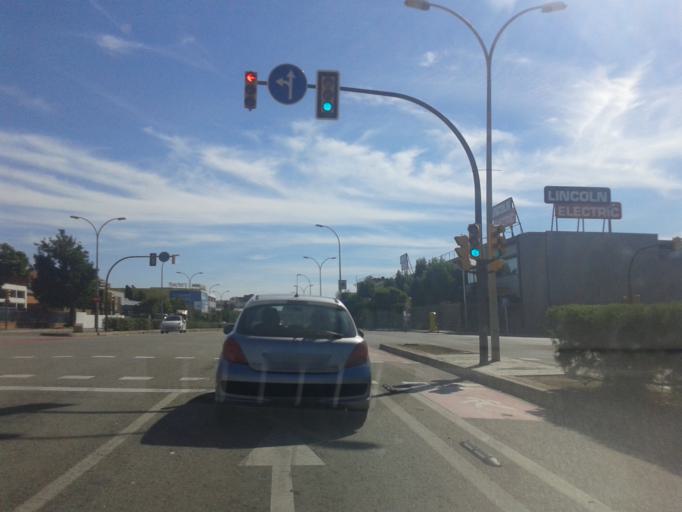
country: ES
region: Catalonia
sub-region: Provincia de Barcelona
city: Sant Feliu de Llobregat
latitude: 41.3909
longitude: 2.0374
